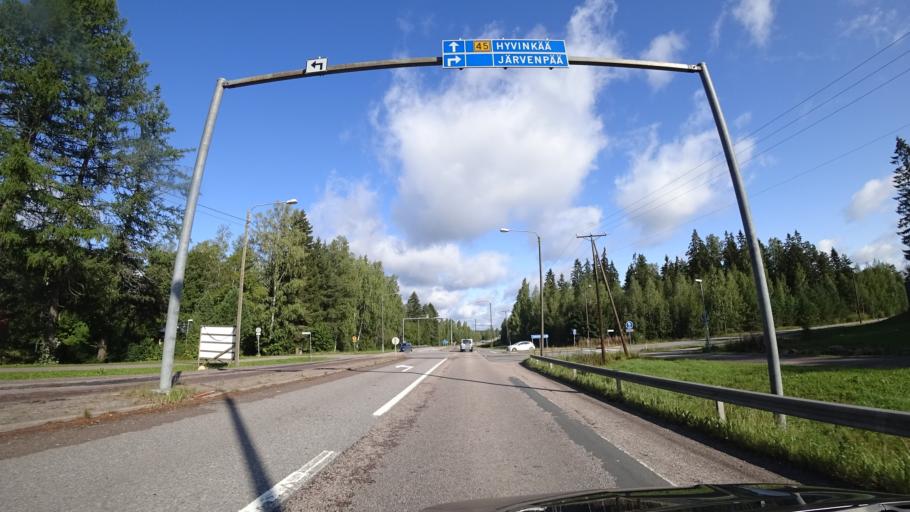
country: FI
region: Uusimaa
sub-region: Helsinki
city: Tuusula
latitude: 60.4147
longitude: 25.0019
